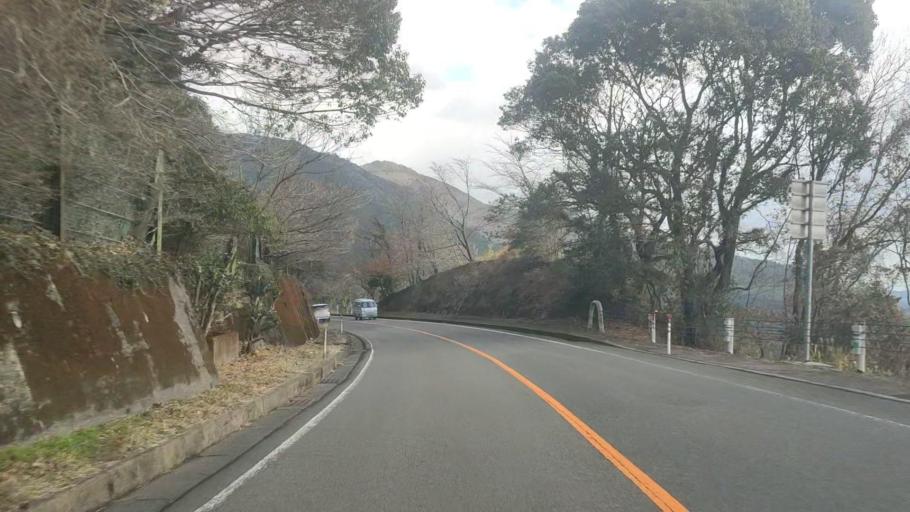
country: JP
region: Kumamoto
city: Hitoyoshi
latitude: 32.0708
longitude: 130.7992
